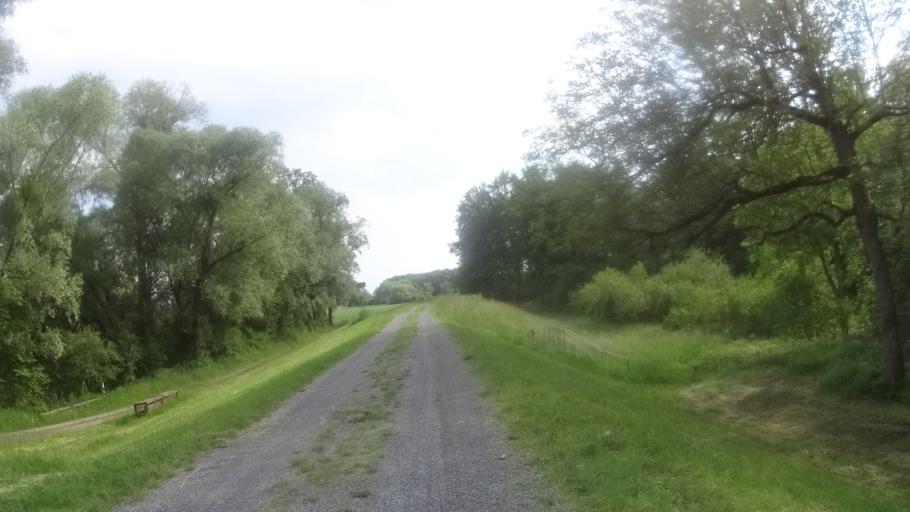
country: DE
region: Baden-Wuerttemberg
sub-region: Karlsruhe Region
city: Hugelsheim
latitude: 48.8123
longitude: 8.1162
